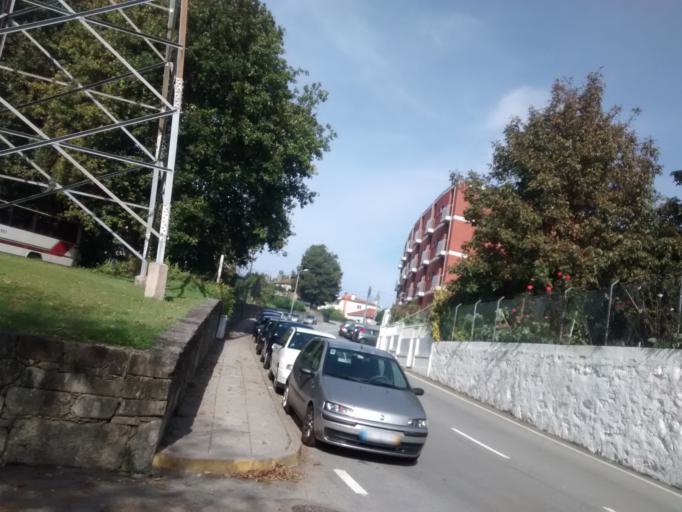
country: PT
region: Braga
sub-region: Braga
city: Adaufe
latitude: 41.5628
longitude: -8.3935
